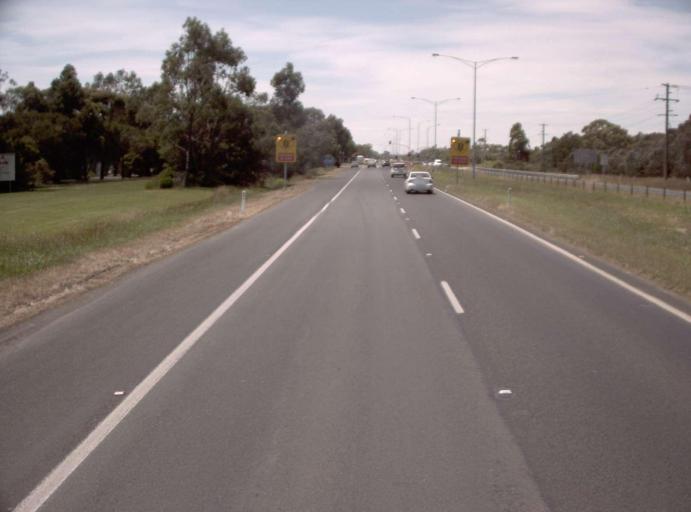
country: AU
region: Victoria
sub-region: Latrobe
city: Morwell
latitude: -38.2223
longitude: 146.4693
